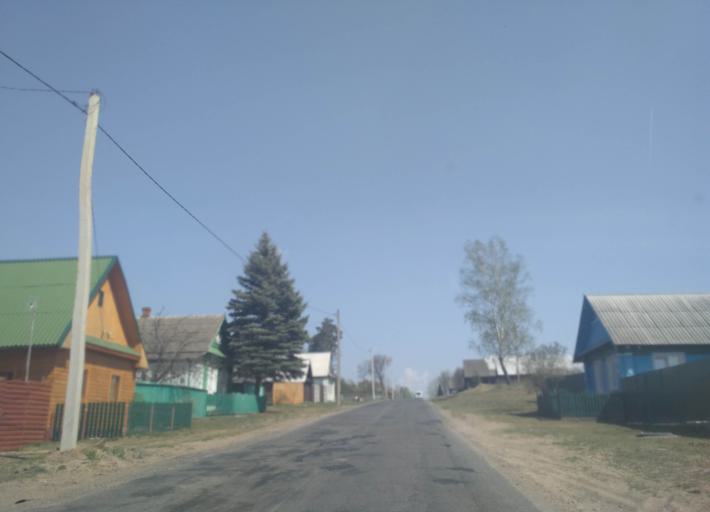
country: BY
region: Minsk
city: Loshnitsa
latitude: 54.4048
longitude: 28.6204
